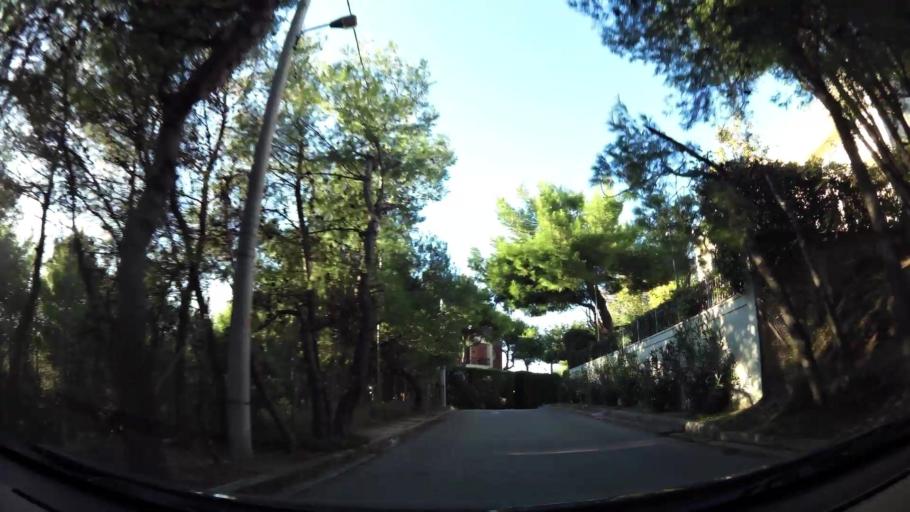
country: GR
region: Attica
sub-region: Nomarchia Athinas
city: Nea Erythraia
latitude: 38.0907
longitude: 23.8292
